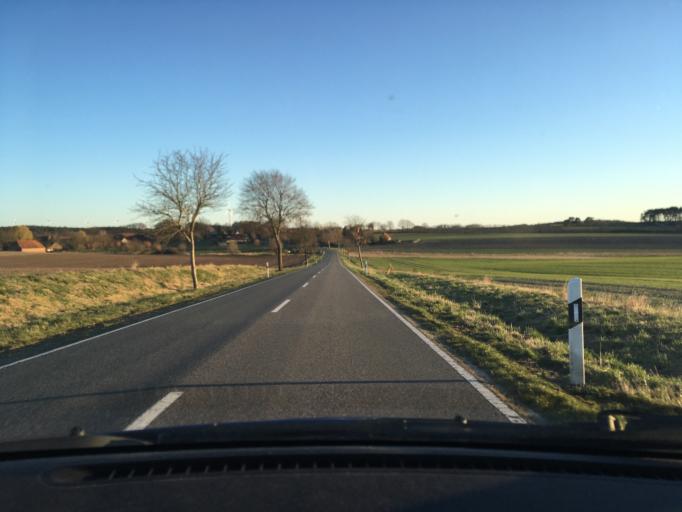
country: DE
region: Lower Saxony
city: Dahlem
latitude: 53.2207
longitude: 10.7546
